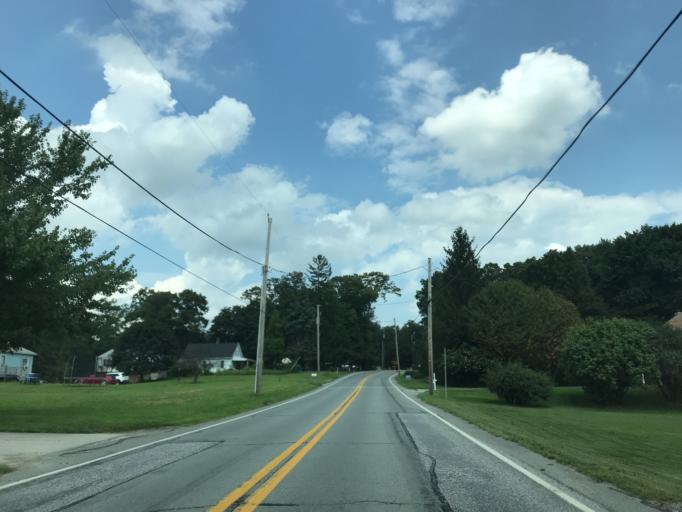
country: US
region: Pennsylvania
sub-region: York County
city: Red Lion
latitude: 39.8826
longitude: -76.6090
